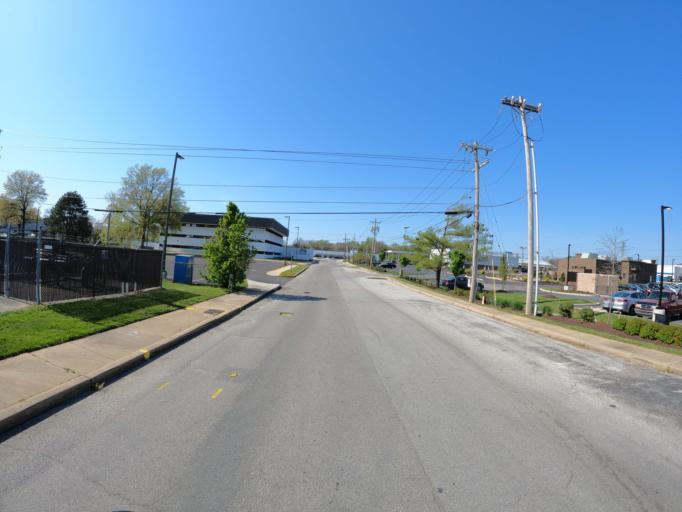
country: US
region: Delaware
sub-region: New Castle County
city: Newark
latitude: 39.6836
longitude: -75.7334
